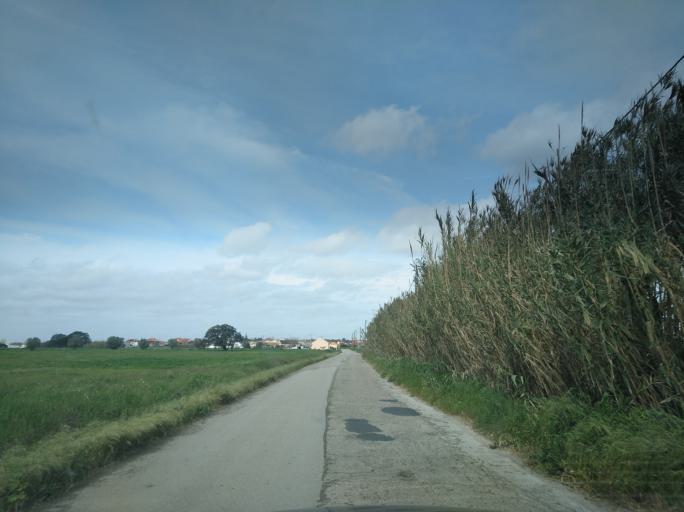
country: PT
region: Setubal
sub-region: Palmela
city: Pinhal Novo
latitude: 38.6690
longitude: -8.9205
